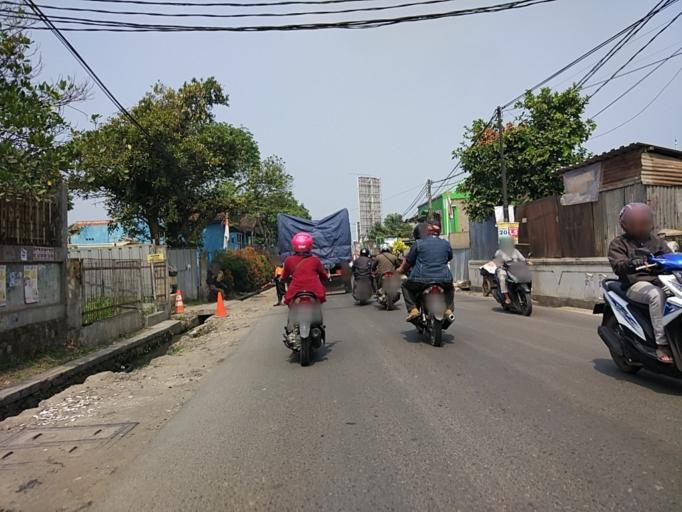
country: ID
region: West Java
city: Padalarang
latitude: -6.8501
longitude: 107.4974
